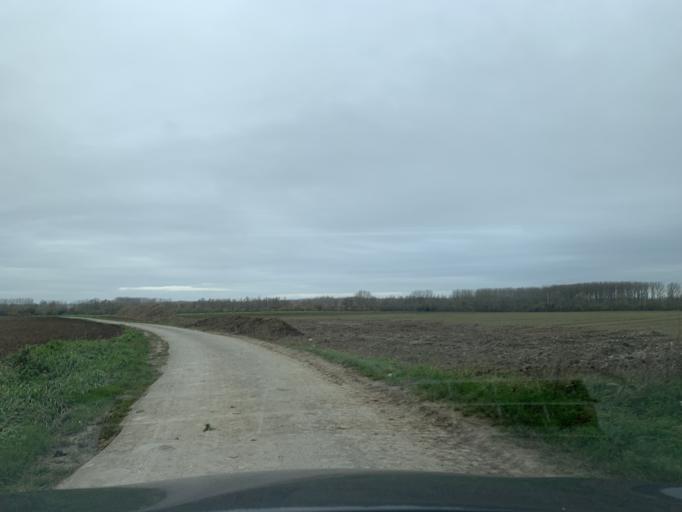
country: FR
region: Nord-Pas-de-Calais
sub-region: Departement du Pas-de-Calais
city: Oisy-le-Verger
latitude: 50.2525
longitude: 3.1090
